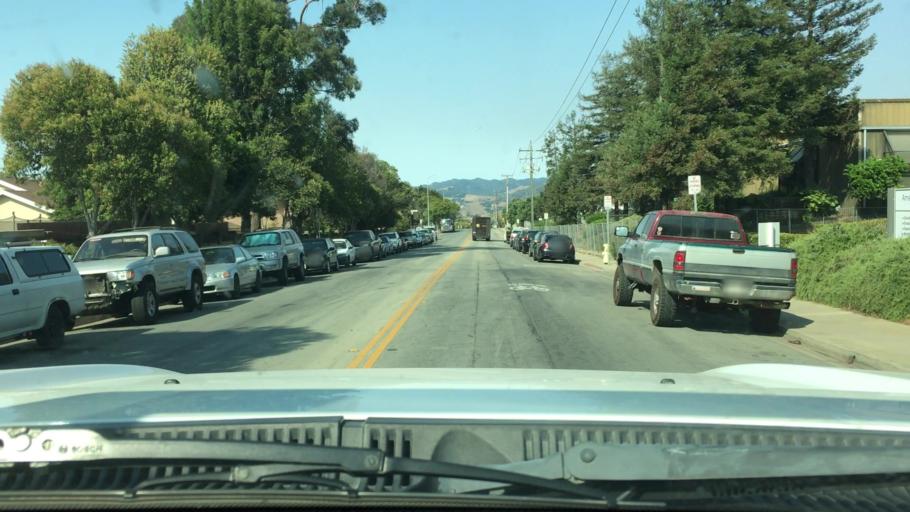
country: US
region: California
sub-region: San Luis Obispo County
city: San Luis Obispo
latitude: 35.2526
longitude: -120.6408
